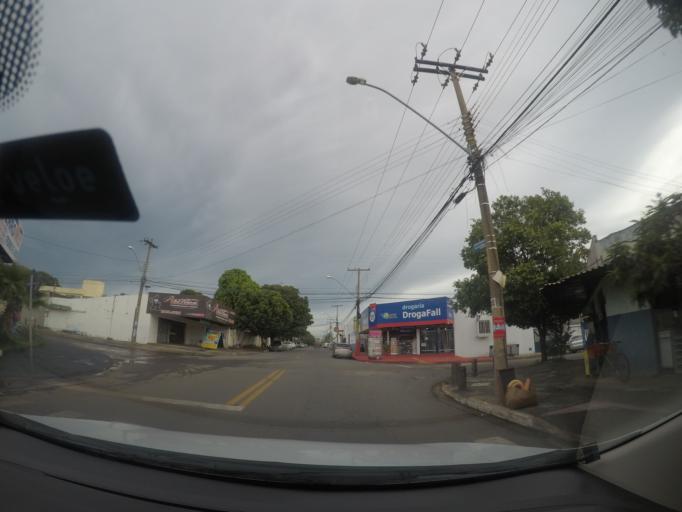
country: BR
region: Goias
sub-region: Goiania
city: Goiania
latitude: -16.7030
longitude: -49.3075
